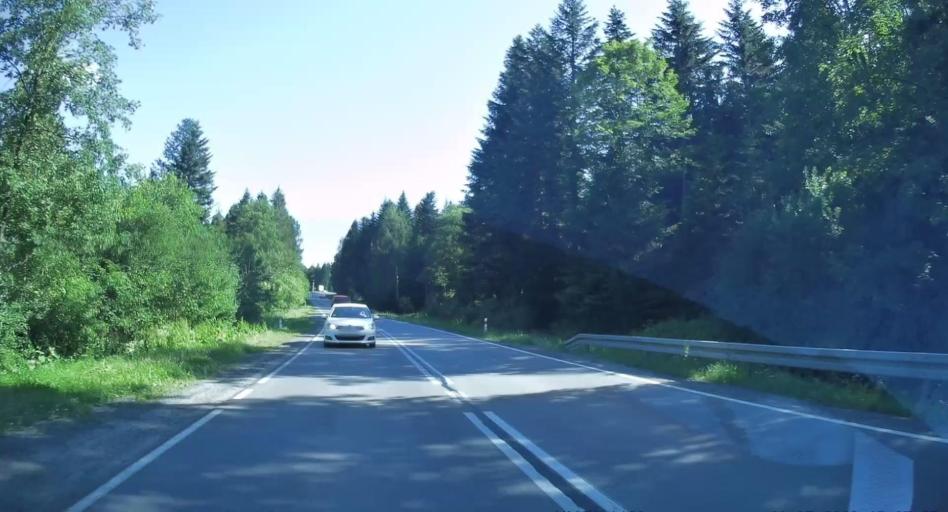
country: PL
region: Lesser Poland Voivodeship
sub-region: Powiat nowosadecki
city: Krynica-Zdroj
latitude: 49.4543
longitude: 20.9526
